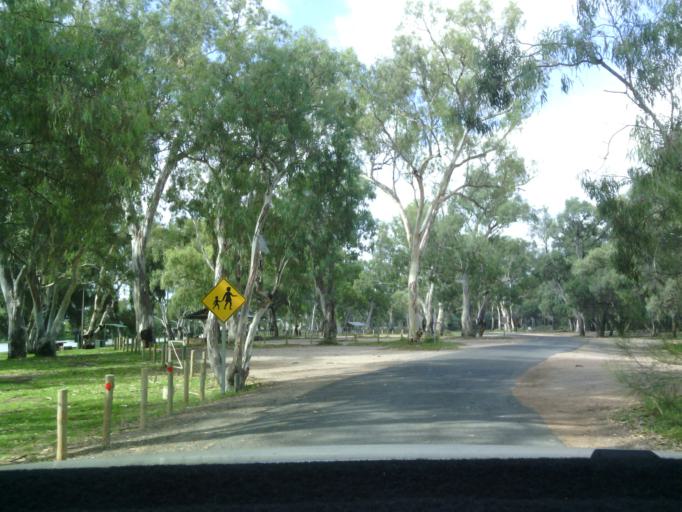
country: AU
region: South Australia
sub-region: Berri and Barmera
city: Berri
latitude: -34.2894
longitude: 140.6313
